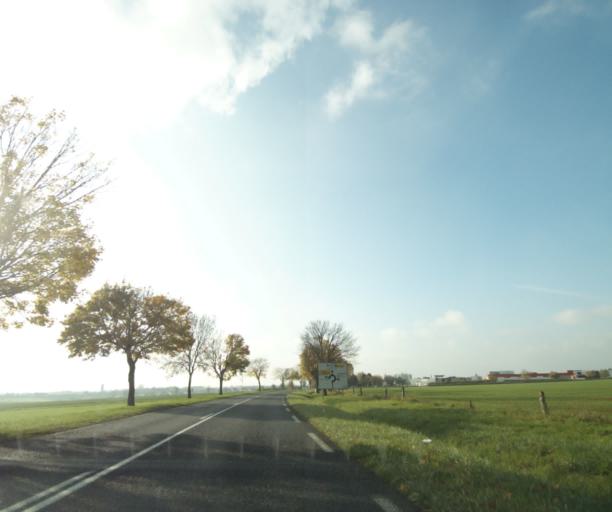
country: FR
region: Lorraine
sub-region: Departement de Meurthe-et-Moselle
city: Briey
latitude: 49.2579
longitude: 5.9499
